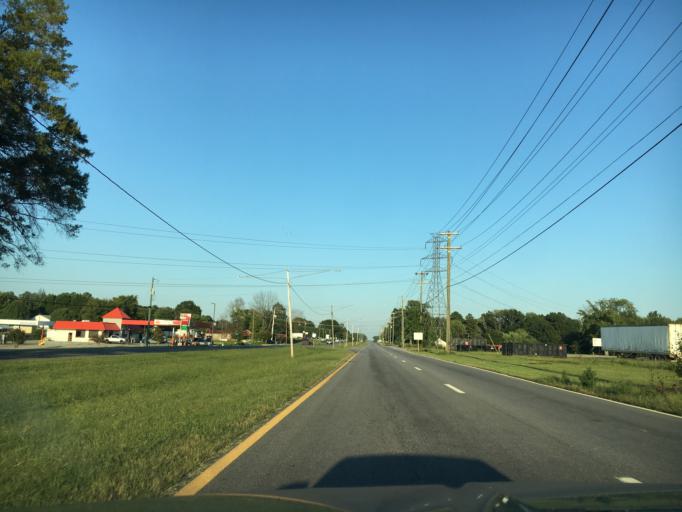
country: US
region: Virginia
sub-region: City of Danville
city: Danville
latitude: 36.5808
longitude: -79.3107
